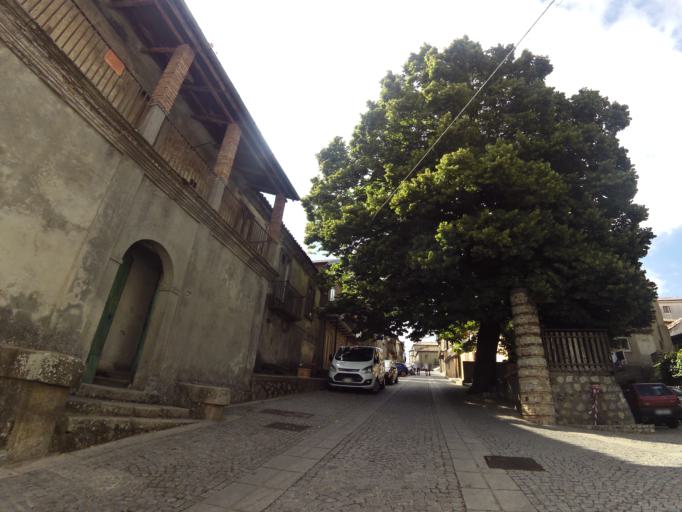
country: IT
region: Calabria
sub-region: Provincia di Vibo-Valentia
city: Mongiana
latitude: 38.5127
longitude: 16.3197
